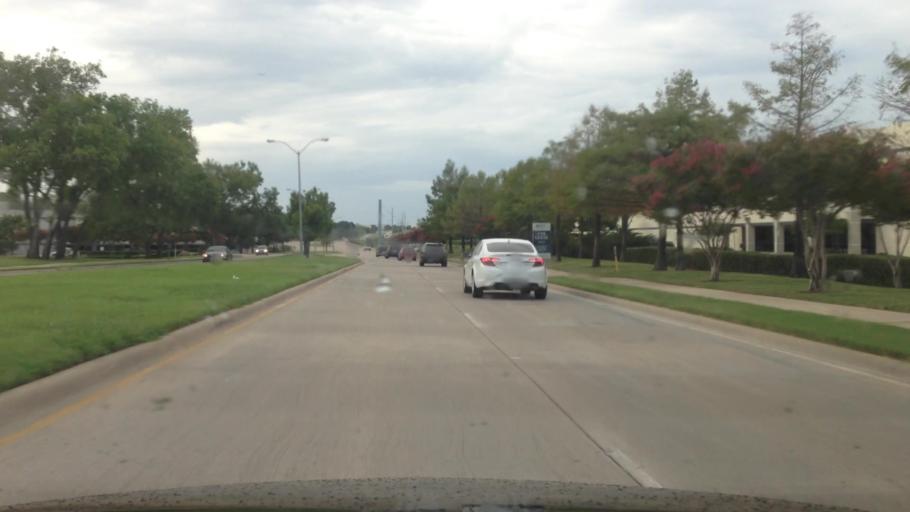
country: US
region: Texas
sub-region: Dallas County
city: Coppell
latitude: 32.9827
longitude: -97.0235
